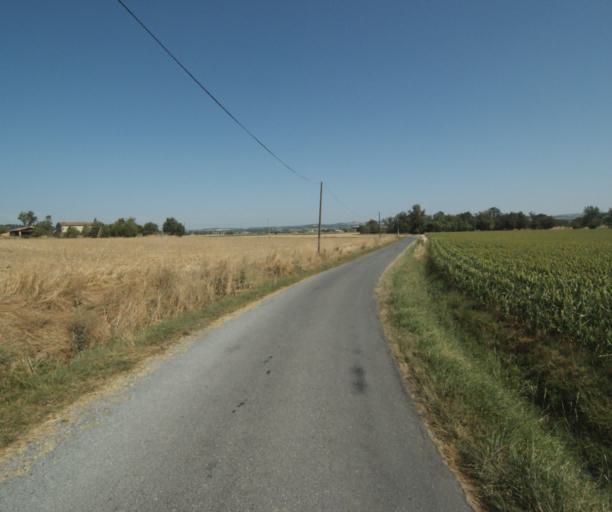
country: FR
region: Midi-Pyrenees
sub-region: Departement de la Haute-Garonne
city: Revel
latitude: 43.5151
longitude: 1.9483
